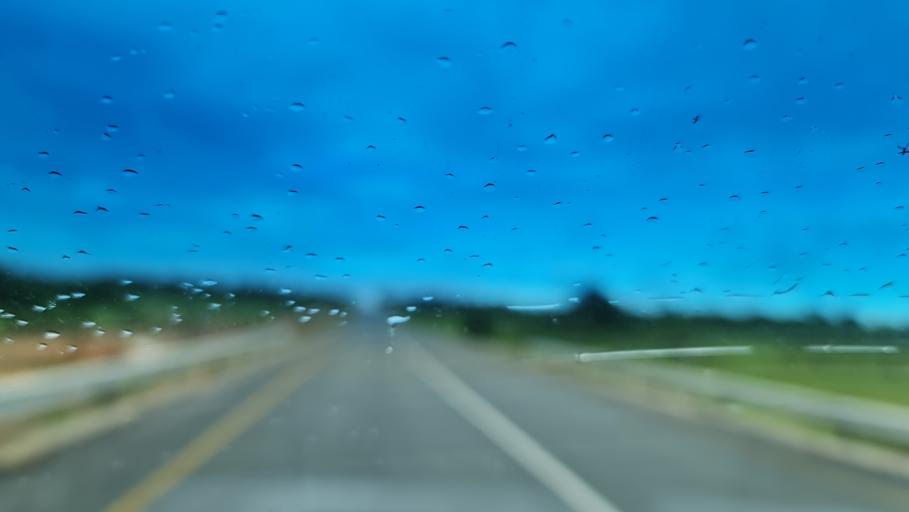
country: MZ
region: Nampula
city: Nampula
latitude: -15.5381
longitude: 39.3291
